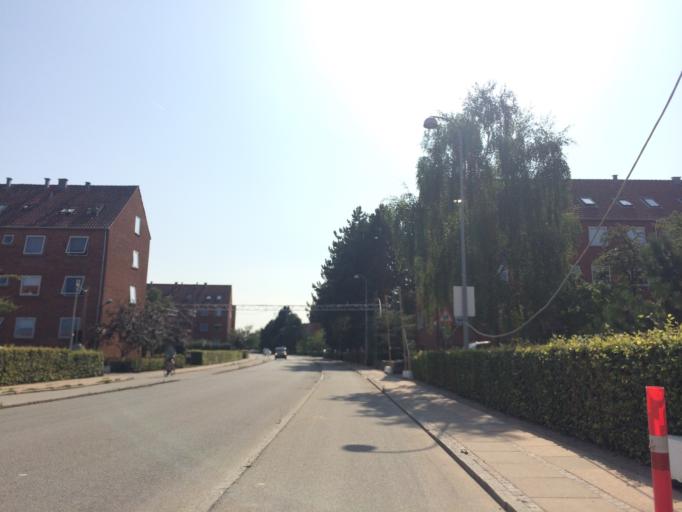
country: DK
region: Capital Region
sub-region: Hvidovre Kommune
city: Hvidovre
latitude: 55.6467
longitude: 12.4741
